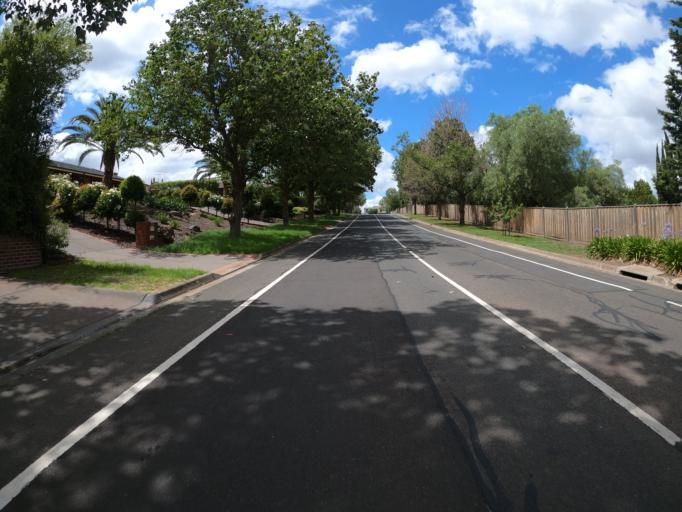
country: AU
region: Victoria
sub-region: Hume
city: Attwood
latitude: -37.6571
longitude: 144.8967
